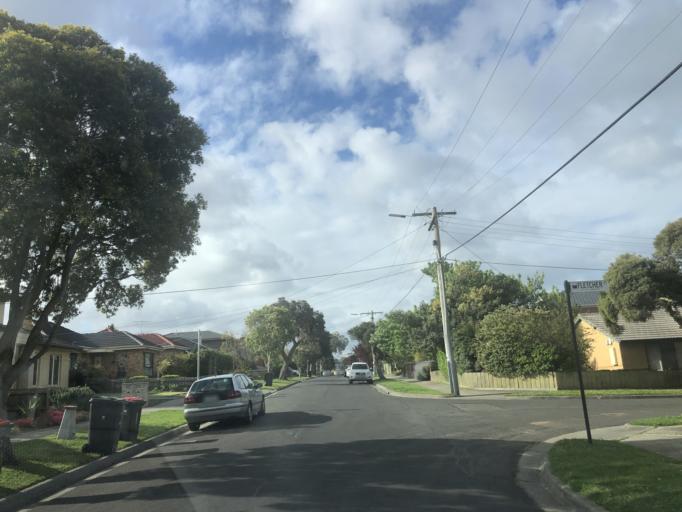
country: AU
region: Victoria
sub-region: Monash
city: Ashwood
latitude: -37.8826
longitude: 145.1159
